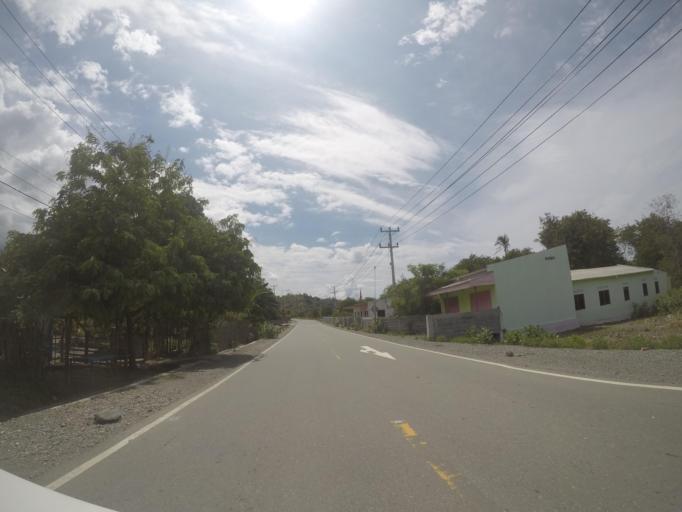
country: TL
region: Liquica
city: Liquica
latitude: -8.5703
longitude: 125.3812
